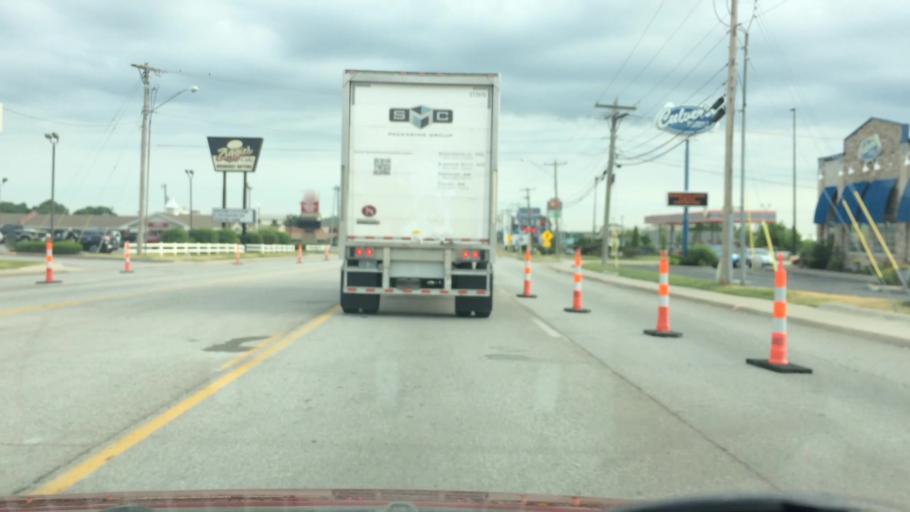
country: US
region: Missouri
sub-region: Greene County
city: Springfield
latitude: 37.2418
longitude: -93.2609
